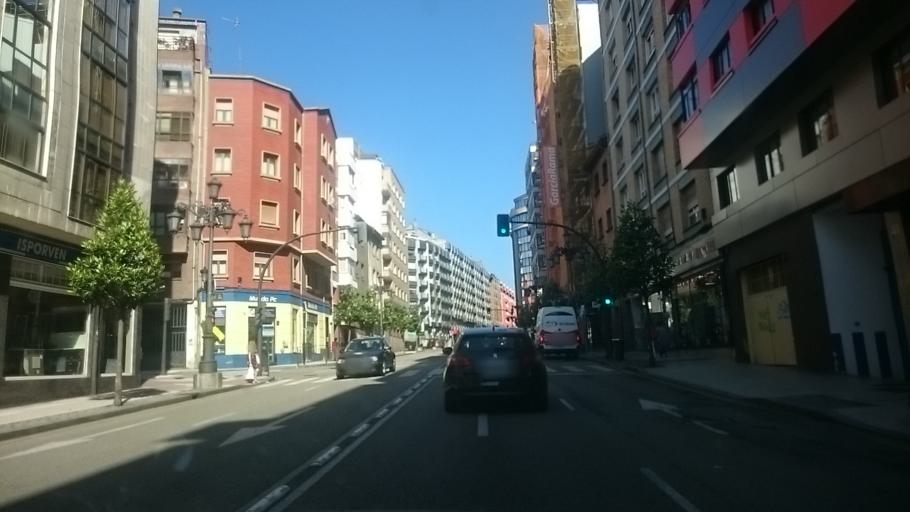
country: ES
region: Asturias
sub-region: Province of Asturias
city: Oviedo
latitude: 43.3561
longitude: -5.8523
